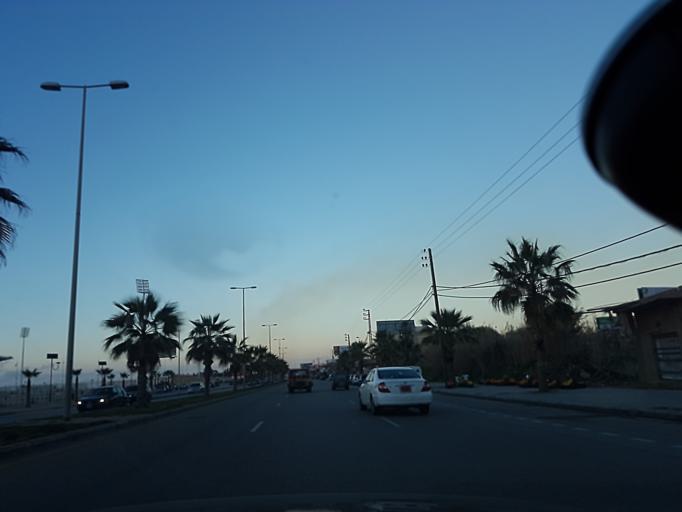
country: LB
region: Liban-Sud
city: Sidon
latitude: 33.5822
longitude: 35.3851
